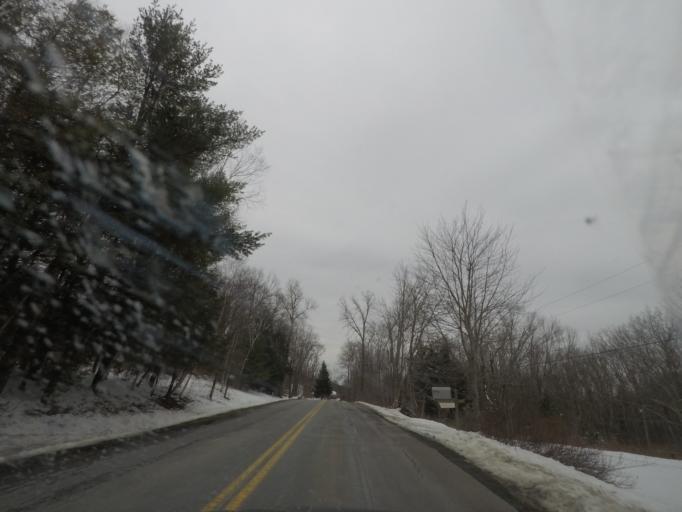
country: US
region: New York
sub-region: Rensselaer County
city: Averill Park
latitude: 42.5757
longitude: -73.4727
